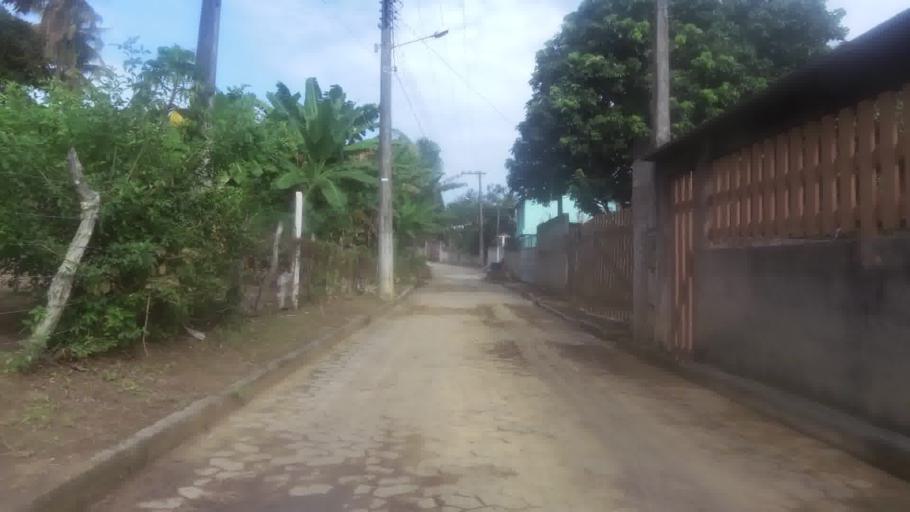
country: BR
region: Espirito Santo
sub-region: Guarapari
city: Guarapari
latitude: -20.7620
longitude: -40.5763
